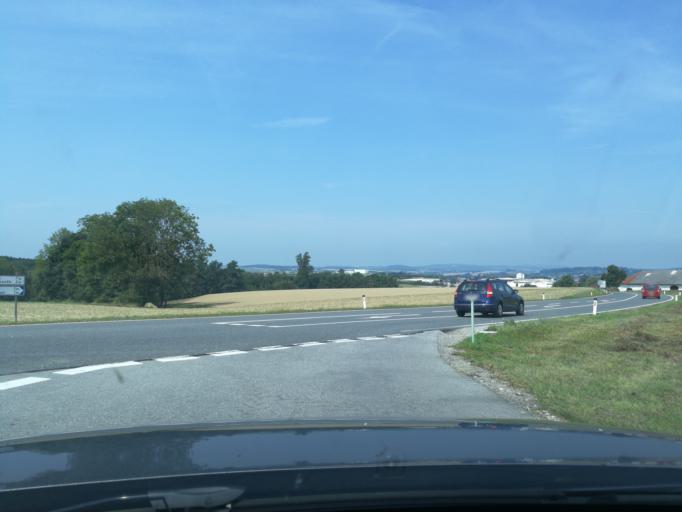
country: AT
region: Upper Austria
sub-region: Politischer Bezirk Grieskirchen
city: Grieskirchen
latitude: 48.3146
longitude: 13.7779
